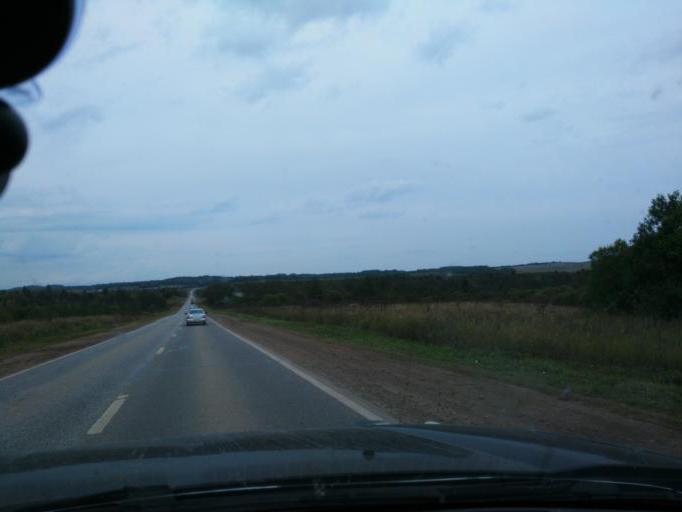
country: RU
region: Perm
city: Chernushka
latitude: 56.5510
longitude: 56.1076
